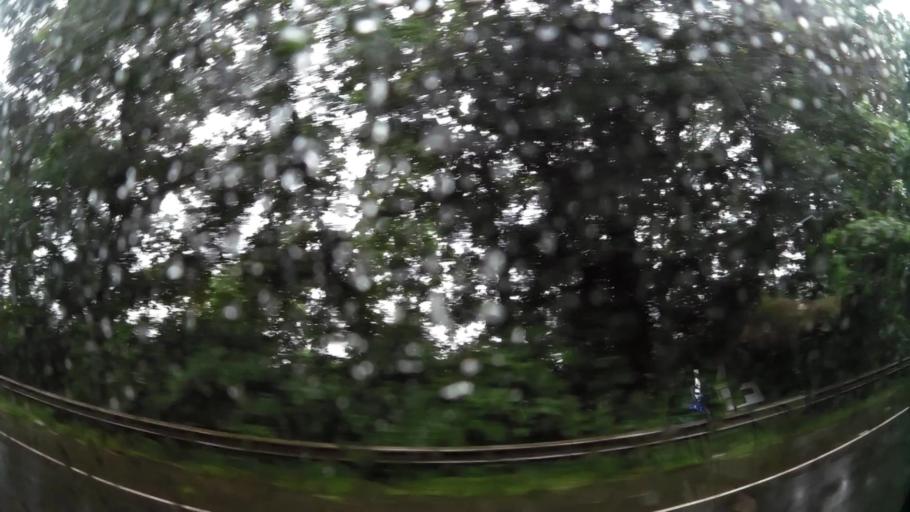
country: PA
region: Colon
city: Quebrada Bonita Adentro
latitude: 9.2859
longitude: -79.7287
